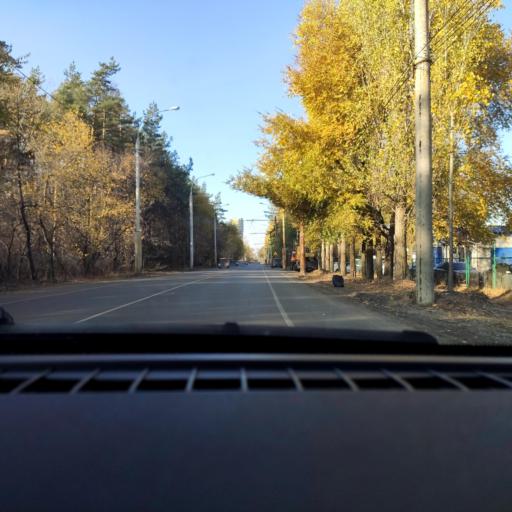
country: RU
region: Voronezj
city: Somovo
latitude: 51.7021
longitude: 39.2880
